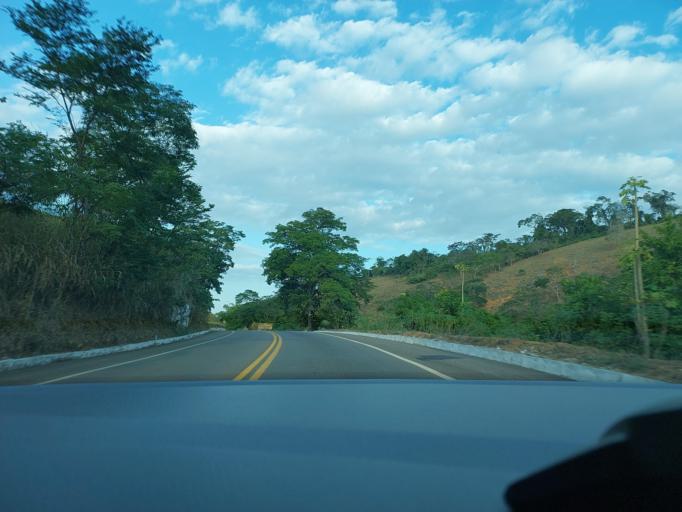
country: BR
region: Minas Gerais
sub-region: Muriae
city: Muriae
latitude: -21.1370
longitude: -42.3128
